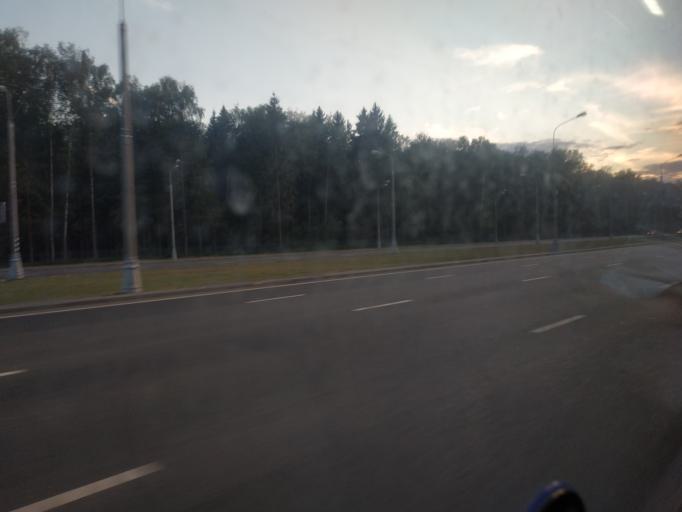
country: RU
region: Moscow
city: Solntsevo
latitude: 55.6057
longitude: 37.4005
